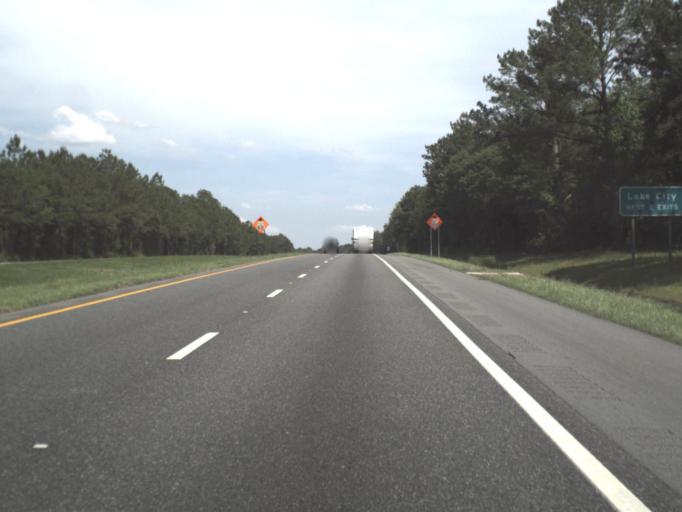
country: US
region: Florida
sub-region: Columbia County
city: Five Points
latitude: 30.2484
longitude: -82.7021
